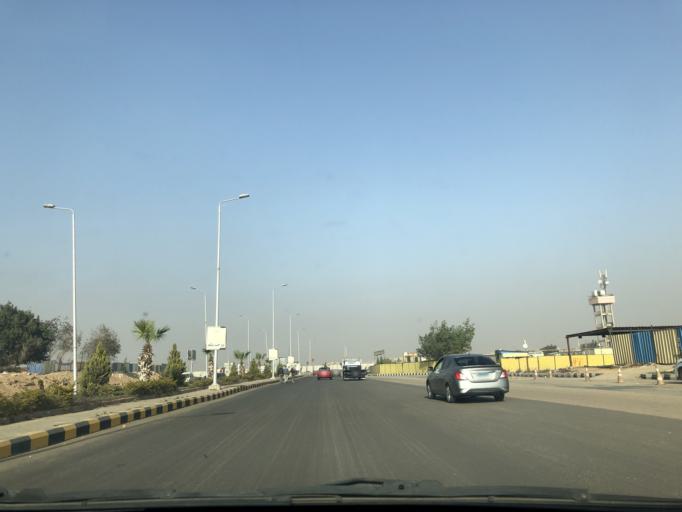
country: EG
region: Al Jizah
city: Madinat Sittah Uktubar
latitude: 29.9542
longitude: 31.0762
